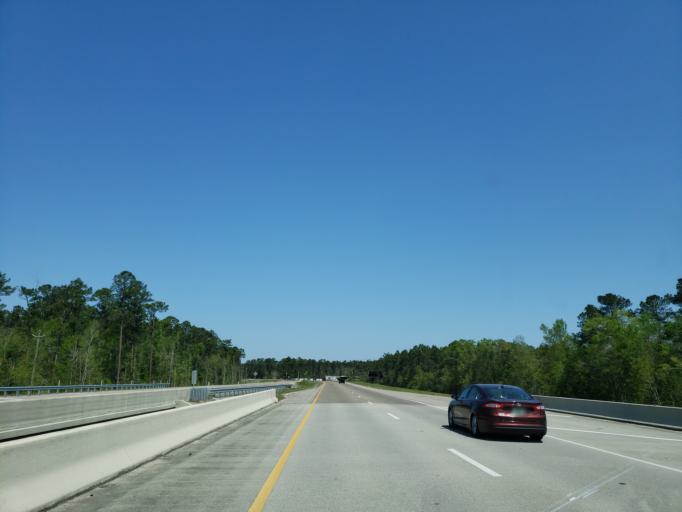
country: US
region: Mississippi
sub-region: Harrison County
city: Lyman
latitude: 30.5231
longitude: -89.1085
